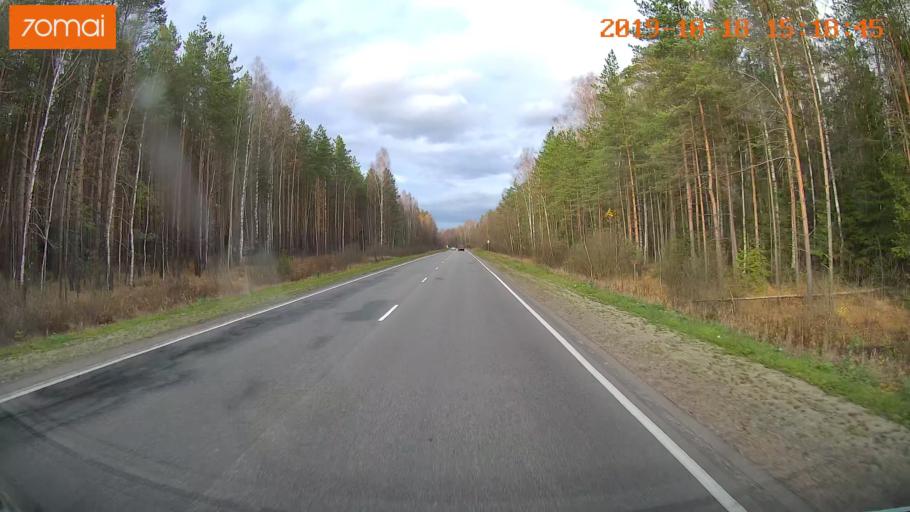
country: RU
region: Vladimir
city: Anopino
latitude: 55.6634
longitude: 40.7319
